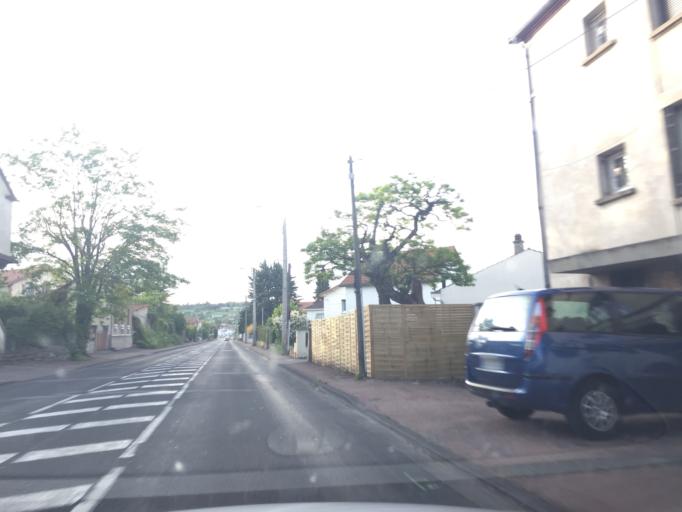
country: FR
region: Auvergne
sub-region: Departement du Puy-de-Dome
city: Riom
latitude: 45.8985
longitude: 3.1059
